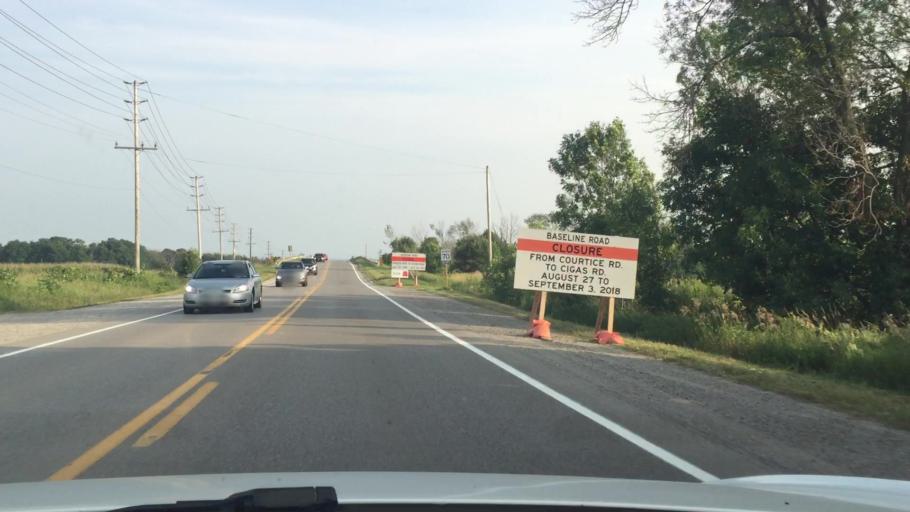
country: CA
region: Ontario
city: Oshawa
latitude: 43.8861
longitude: -78.7668
